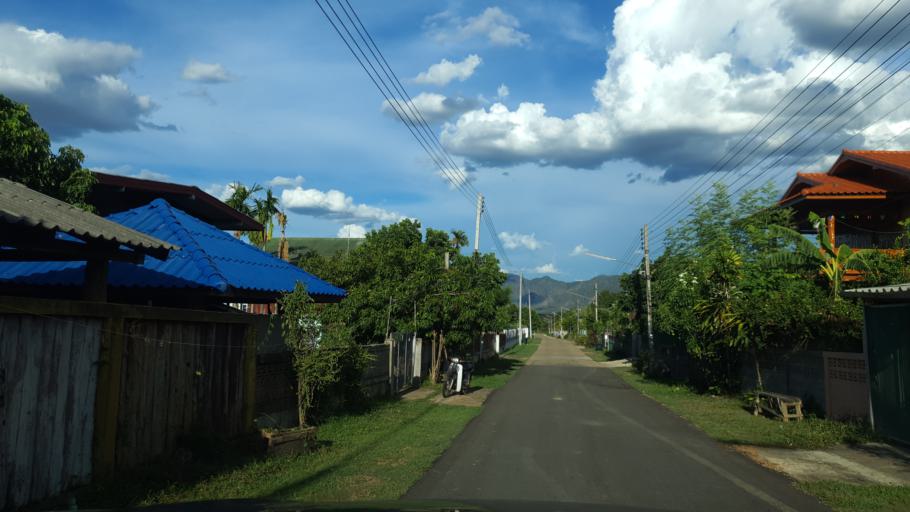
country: TH
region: Lampang
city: Sop Prap
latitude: 17.8758
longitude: 99.3006
